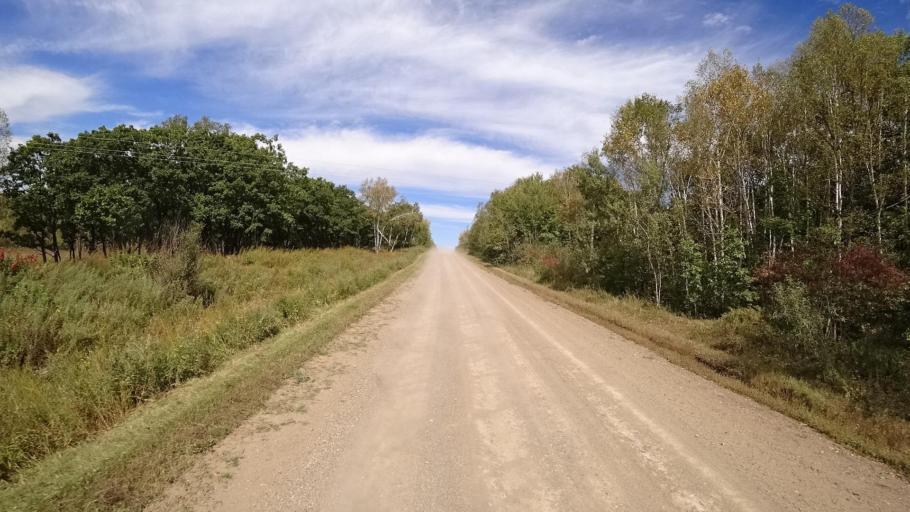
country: RU
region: Primorskiy
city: Yakovlevka
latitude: 44.6813
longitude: 133.6172
